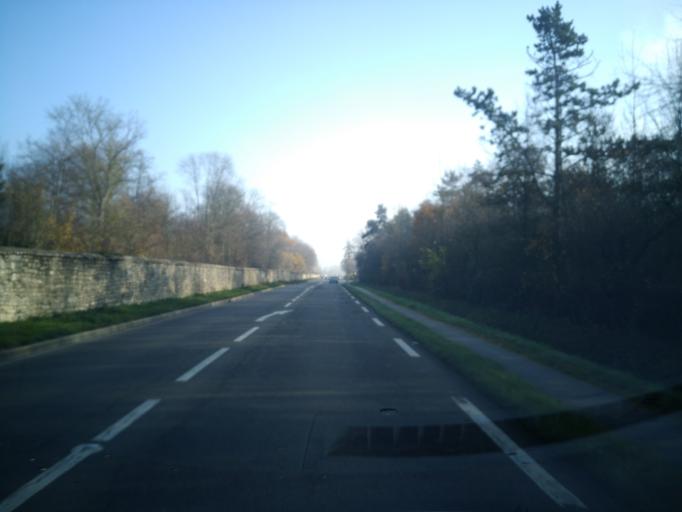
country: FR
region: Ile-de-France
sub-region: Departement des Yvelines
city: Thiverval-Grignon
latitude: 48.8427
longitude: 1.9326
